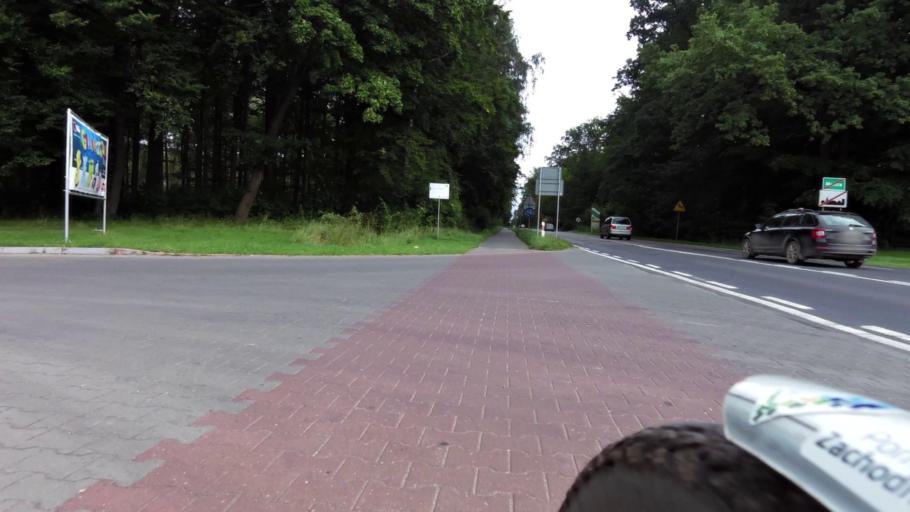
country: PL
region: West Pomeranian Voivodeship
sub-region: Koszalin
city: Koszalin
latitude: 54.2169
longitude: 16.1144
